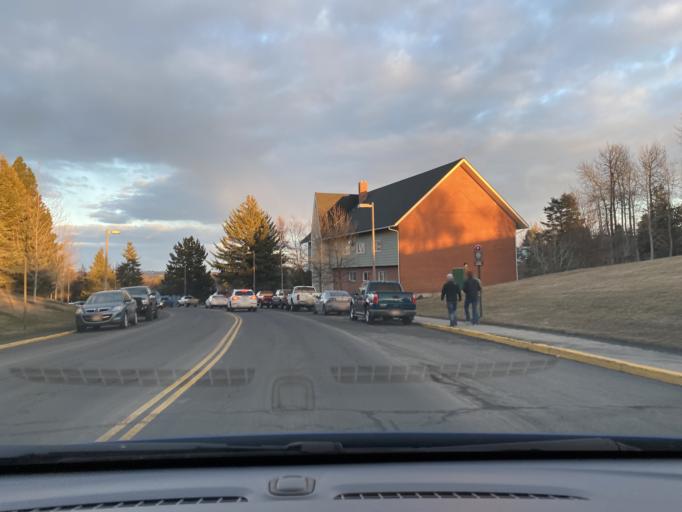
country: US
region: Idaho
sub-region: Latah County
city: Moscow
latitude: 46.7232
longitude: -117.0135
